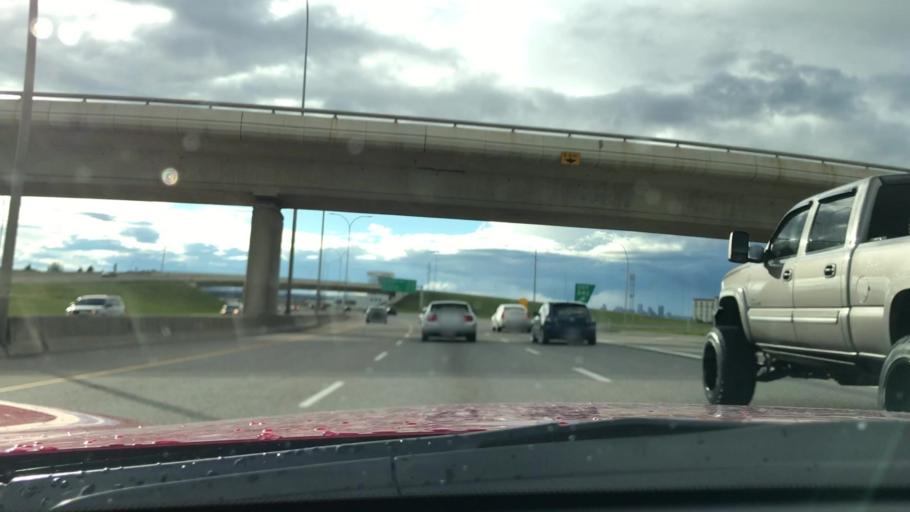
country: CA
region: Alberta
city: Calgary
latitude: 50.9432
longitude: -113.9792
